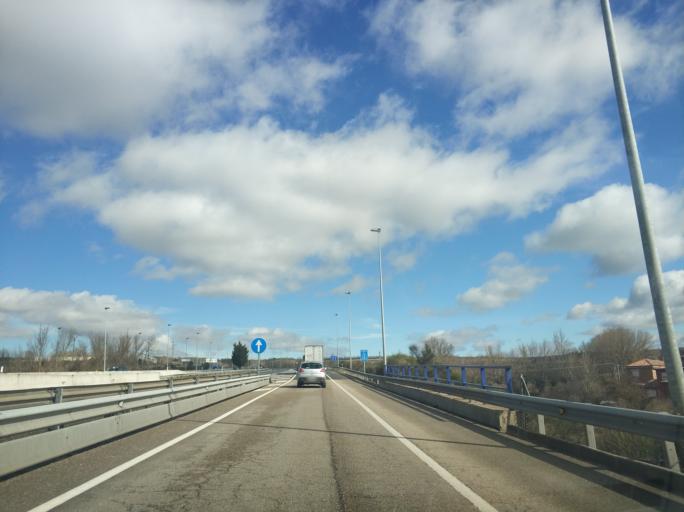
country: ES
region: Castille and Leon
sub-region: Provincia de Burgos
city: Saldana de Burgos
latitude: 42.2650
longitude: -3.6987
